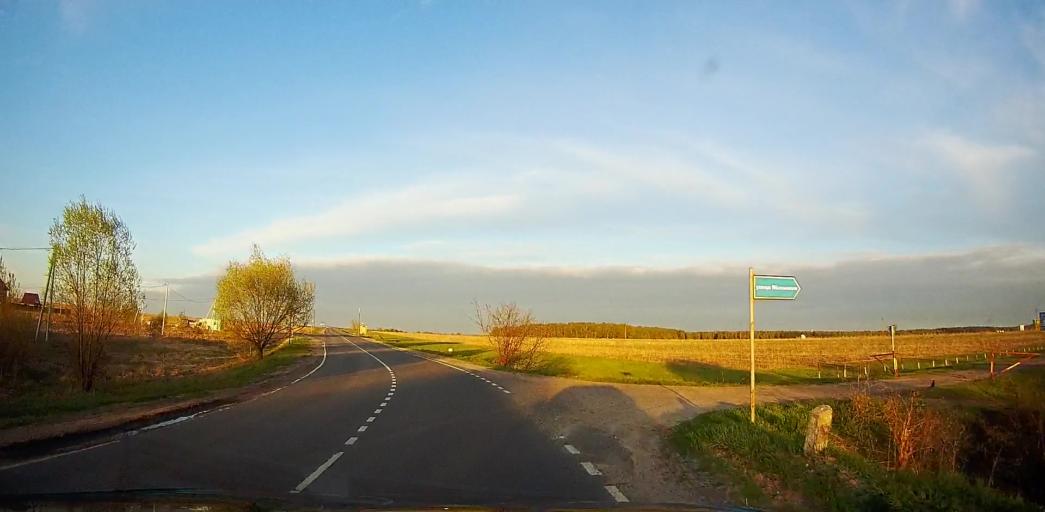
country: RU
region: Moskovskaya
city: Peski
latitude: 55.2101
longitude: 38.6760
